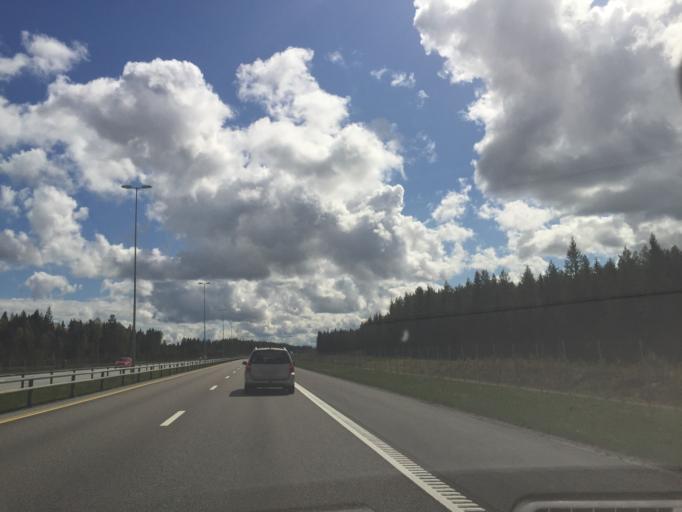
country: NO
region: Akershus
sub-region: Eidsvoll
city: Raholt
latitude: 60.2119
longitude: 11.1839
